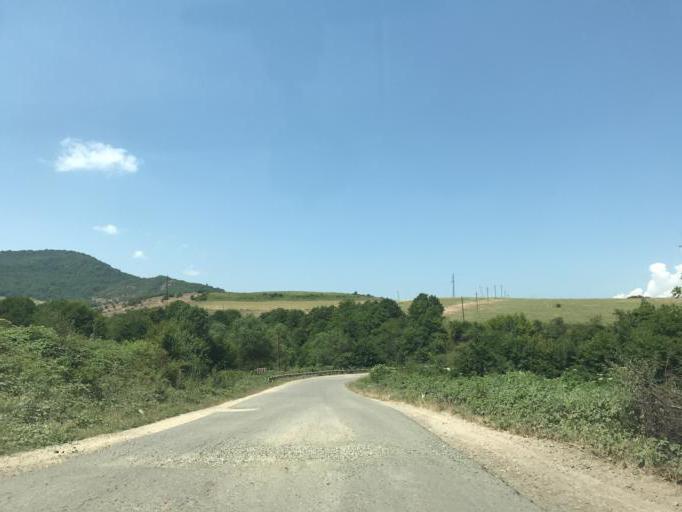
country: AZ
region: Tartar Rayon
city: Martakert
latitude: 40.1092
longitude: 46.6360
